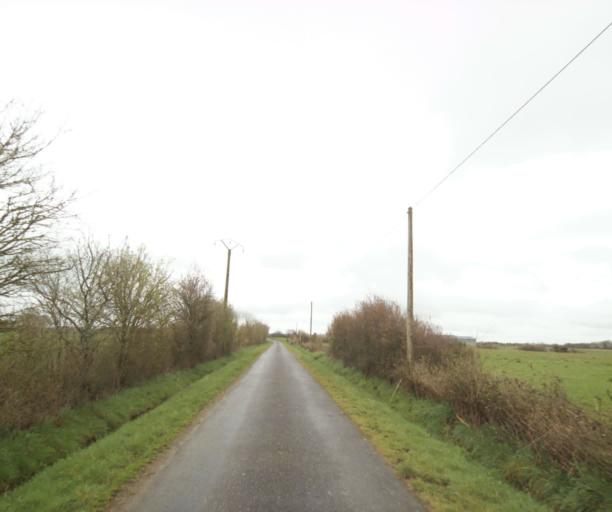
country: FR
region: Pays de la Loire
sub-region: Departement de la Loire-Atlantique
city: Bouvron
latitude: 47.4530
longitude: -1.8933
